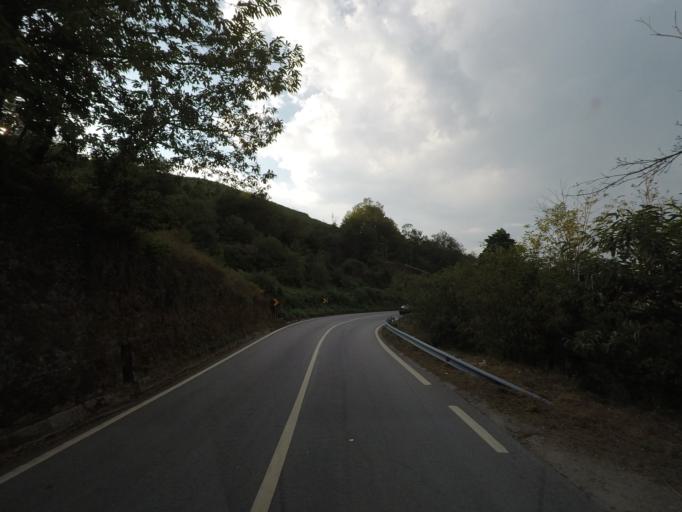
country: PT
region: Porto
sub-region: Baiao
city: Valadares
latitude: 41.1923
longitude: -7.9460
